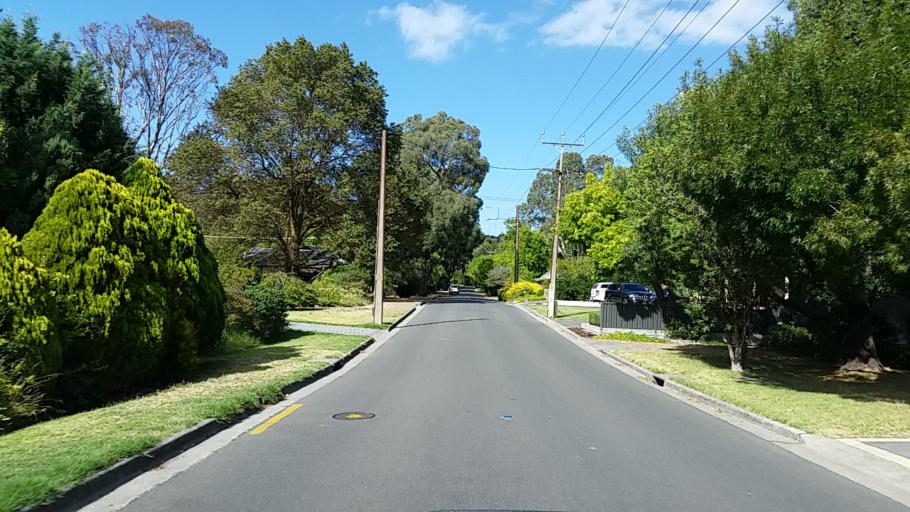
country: AU
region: South Australia
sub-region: Mount Barker
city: Hahndorf
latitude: -35.0307
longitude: 138.8166
